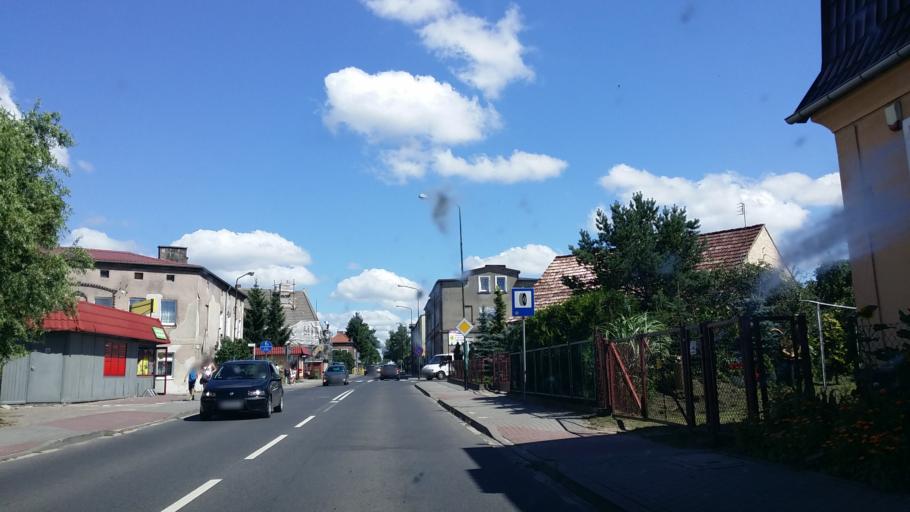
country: PL
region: West Pomeranian Voivodeship
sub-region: Powiat swidwinski
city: Swidwin
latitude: 53.7782
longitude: 15.7778
